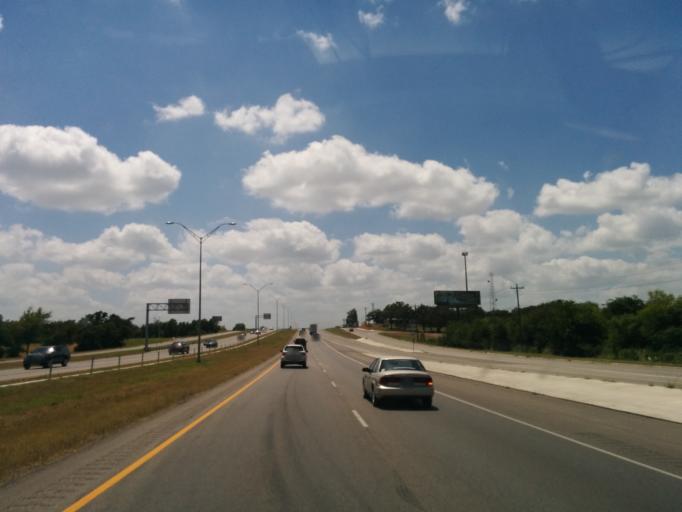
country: US
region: Texas
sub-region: Bastrop County
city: Bastrop
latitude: 30.1112
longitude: -97.3616
